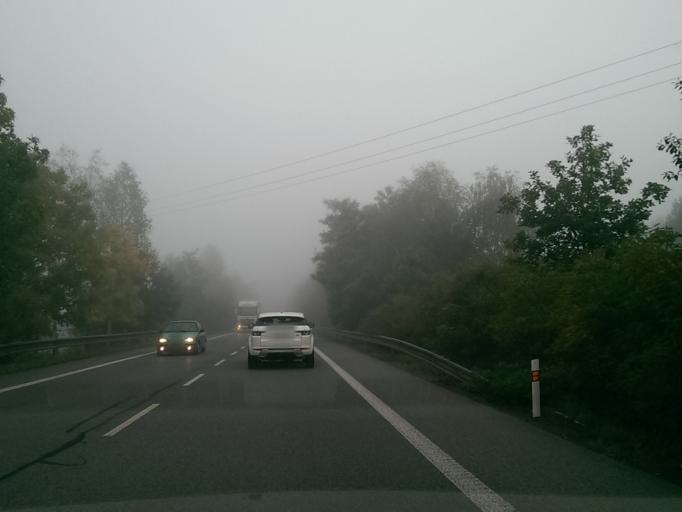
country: CZ
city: Doksy
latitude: 50.5750
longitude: 14.6404
